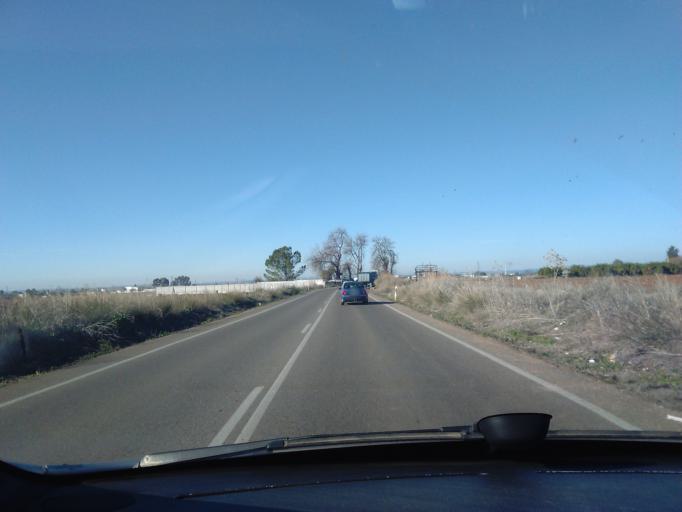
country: ES
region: Andalusia
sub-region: Provincia de Sevilla
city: Sevilla
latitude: 37.4366
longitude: -5.9388
